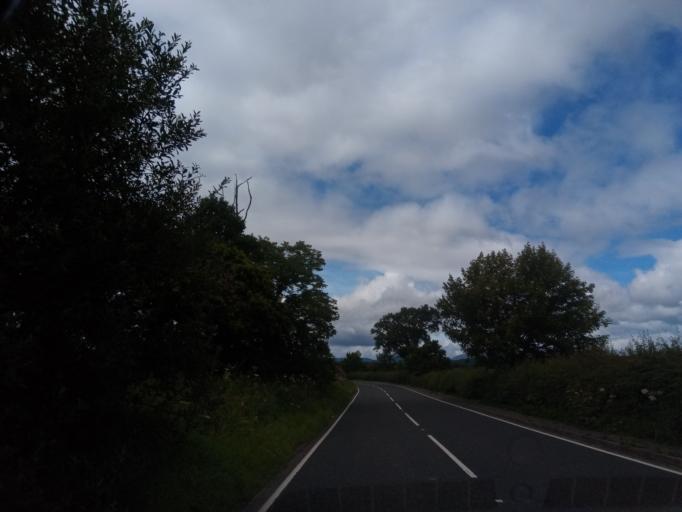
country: GB
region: Scotland
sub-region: Stirling
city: Doune
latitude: 56.1866
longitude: -4.0267
